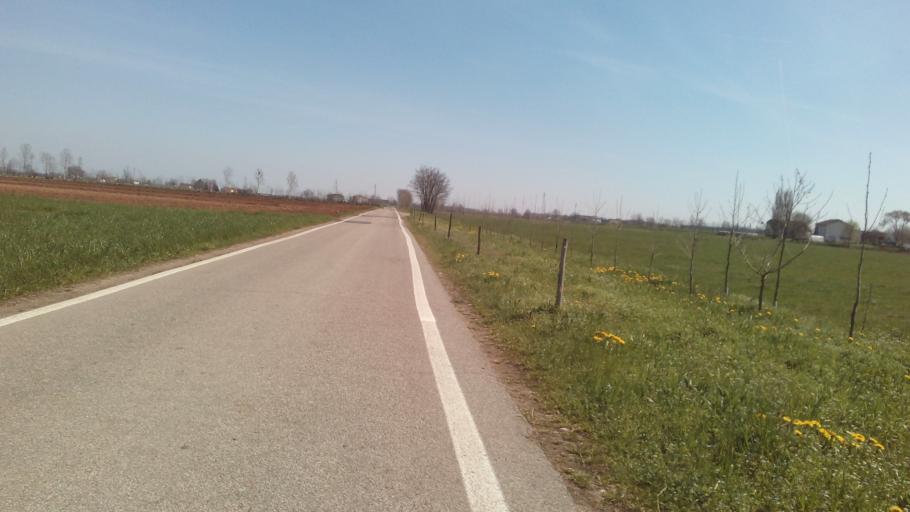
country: IT
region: Lombardy
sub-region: Provincia di Mantova
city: Cerlongo
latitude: 45.2861
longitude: 10.6776
